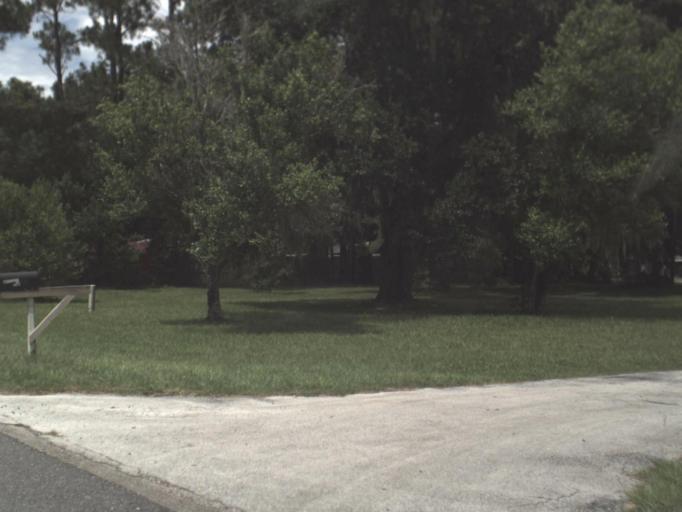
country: US
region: Florida
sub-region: Citrus County
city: Hernando
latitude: 28.9490
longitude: -82.3775
